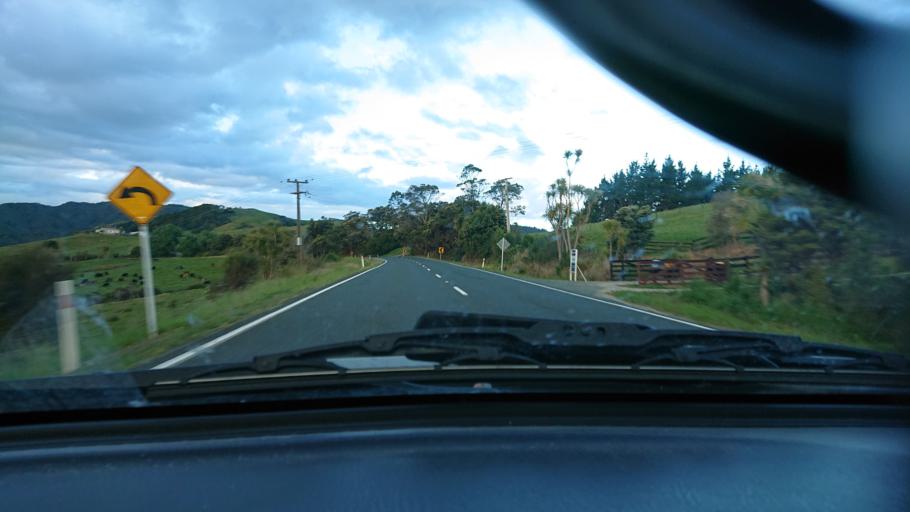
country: NZ
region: Auckland
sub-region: Auckland
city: Parakai
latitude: -36.4739
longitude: 174.4489
